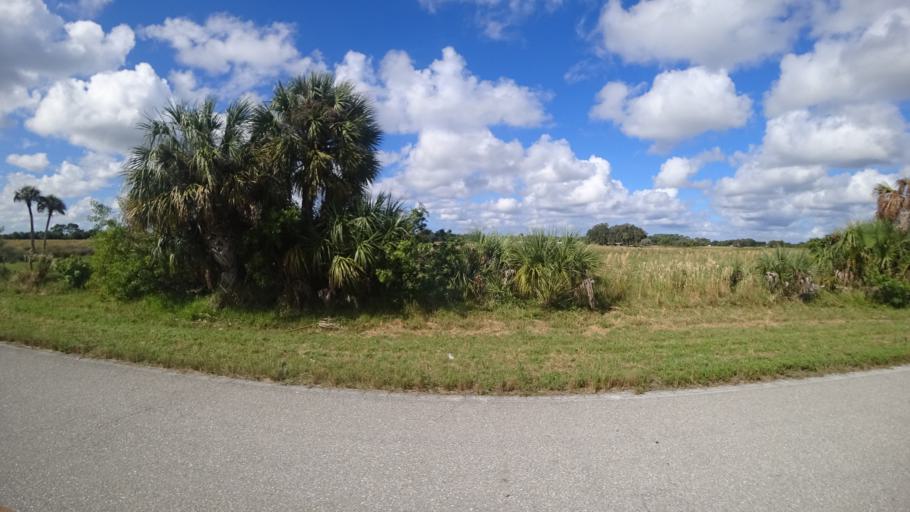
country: US
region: Florida
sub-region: Manatee County
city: Ellenton
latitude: 27.6119
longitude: -82.4818
